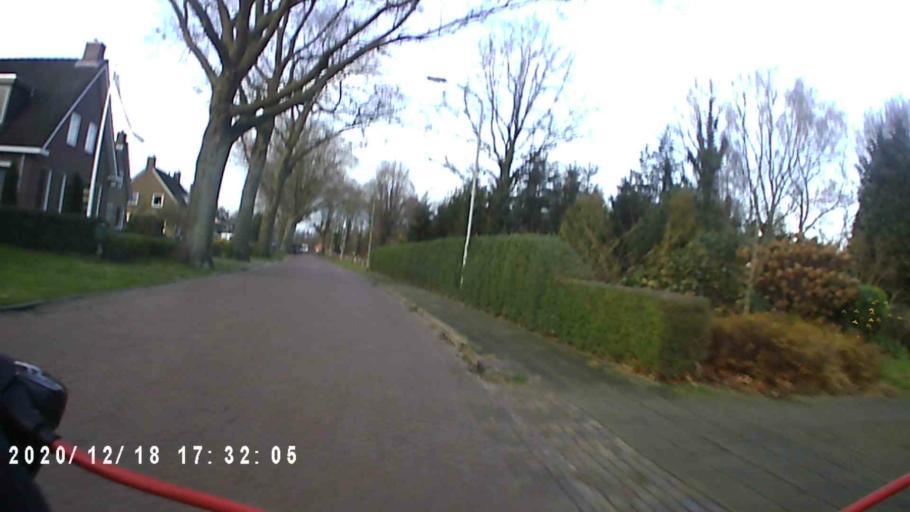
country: NL
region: Drenthe
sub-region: Gemeente Tynaarlo
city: Vries
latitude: 53.0801
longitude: 6.5754
